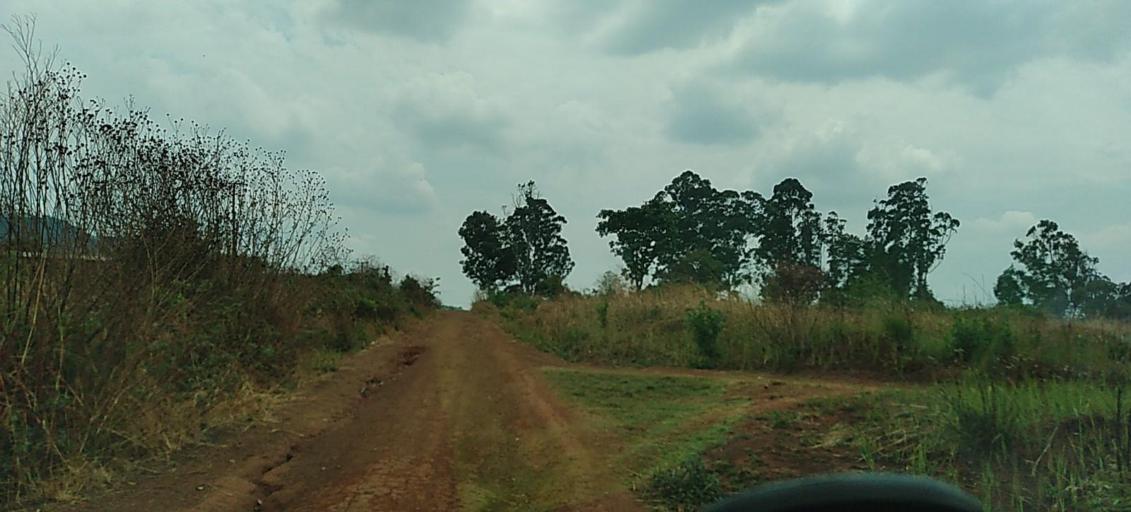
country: ZM
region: North-Western
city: Kansanshi
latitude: -12.0324
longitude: 26.4352
